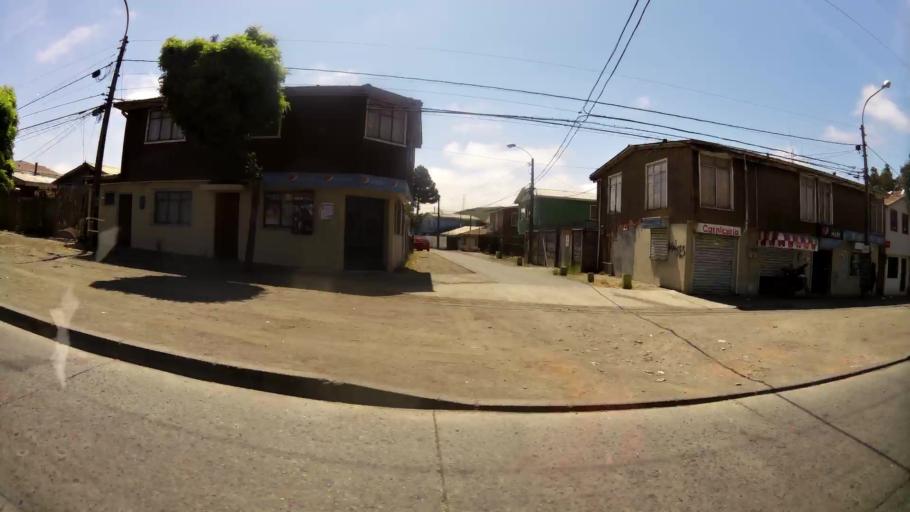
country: CL
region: Biobio
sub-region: Provincia de Concepcion
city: Concepcion
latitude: -36.8057
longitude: -73.0438
